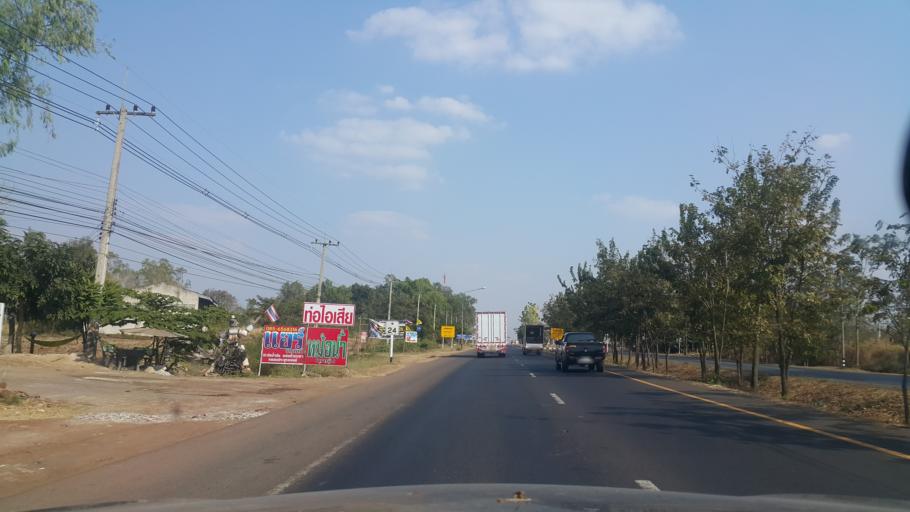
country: TH
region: Buriram
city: Nong Ki
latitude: 14.6898
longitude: 102.5209
